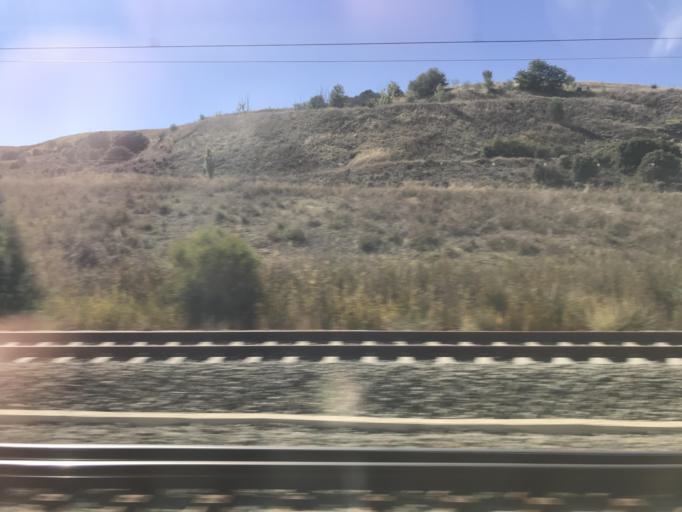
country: ES
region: Castille-La Mancha
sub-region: Provincia de Cuenca
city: Cuenca
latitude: 40.0366
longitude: -2.1467
